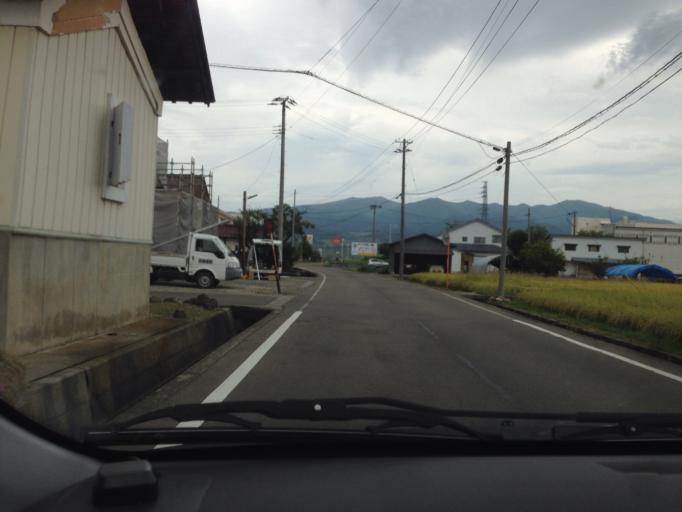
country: JP
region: Fukushima
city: Kitakata
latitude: 37.6314
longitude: 139.8918
